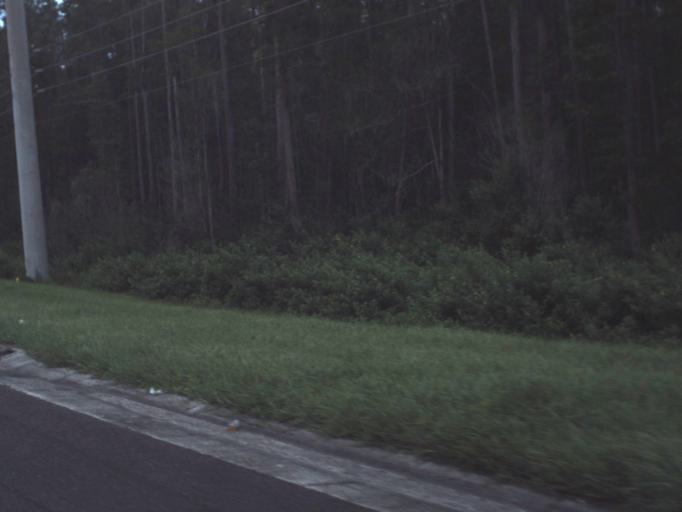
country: US
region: Florida
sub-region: Pasco County
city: Odessa
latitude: 28.1854
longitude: -82.5618
